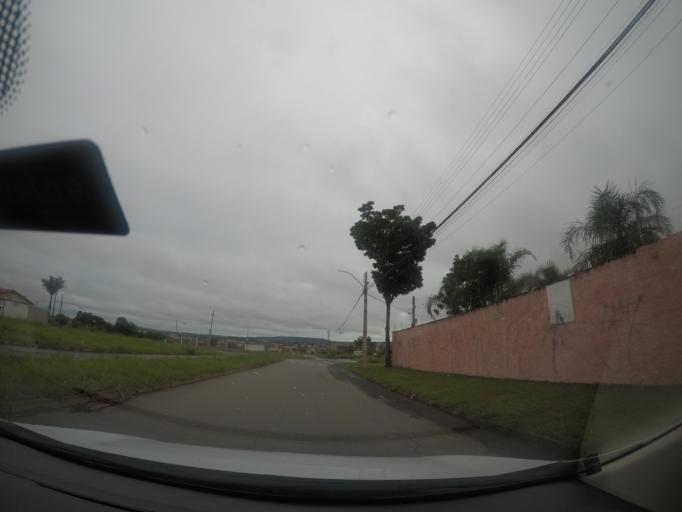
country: BR
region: Goias
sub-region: Goiania
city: Goiania
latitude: -16.7534
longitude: -49.3176
